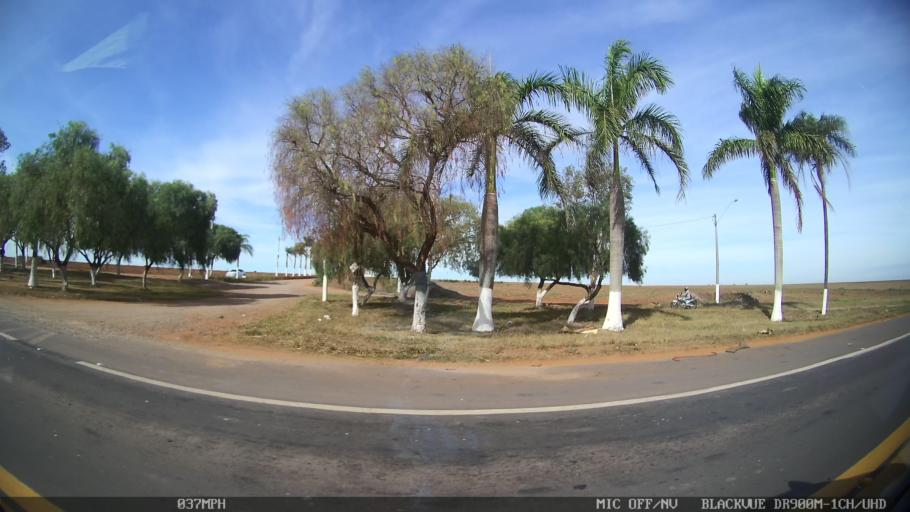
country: BR
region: Sao Paulo
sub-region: Rio Das Pedras
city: Rio das Pedras
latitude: -22.7949
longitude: -47.5889
